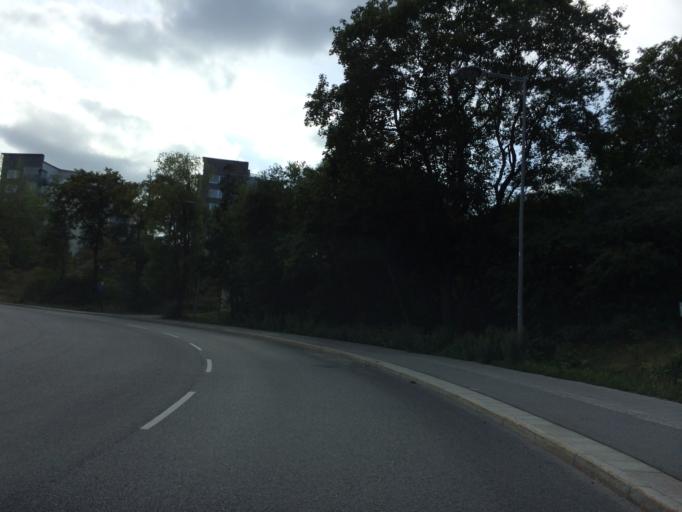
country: SE
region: Stockholm
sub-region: Stockholms Kommun
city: Arsta
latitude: 59.3043
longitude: 18.0289
